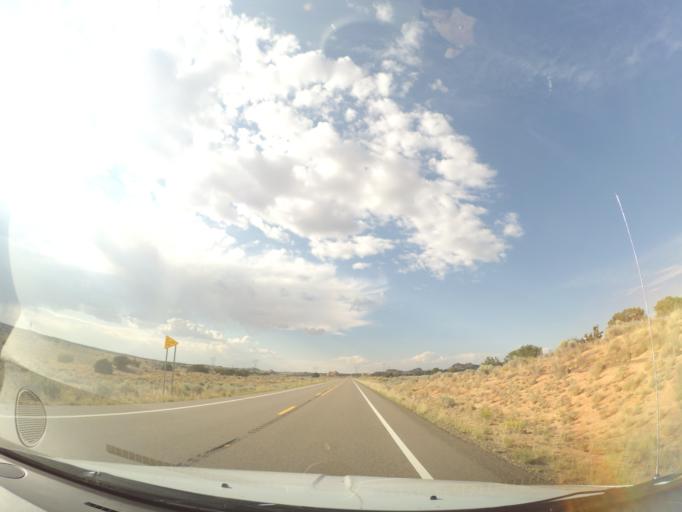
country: US
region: Arizona
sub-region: Coconino County
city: LeChee
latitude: 36.5960
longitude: -111.4260
